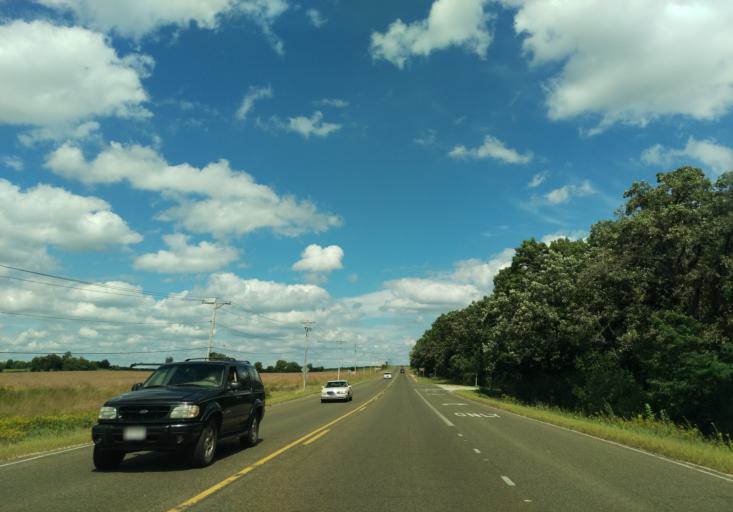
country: US
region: Wisconsin
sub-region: Dane County
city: Shorewood Hills
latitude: 43.1221
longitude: -89.4420
